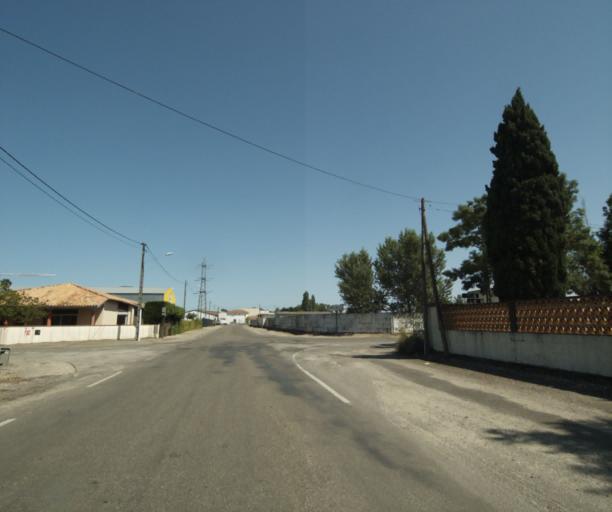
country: FR
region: Midi-Pyrenees
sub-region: Departement du Tarn-et-Garonne
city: Montauban
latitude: 44.0407
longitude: 1.3648
